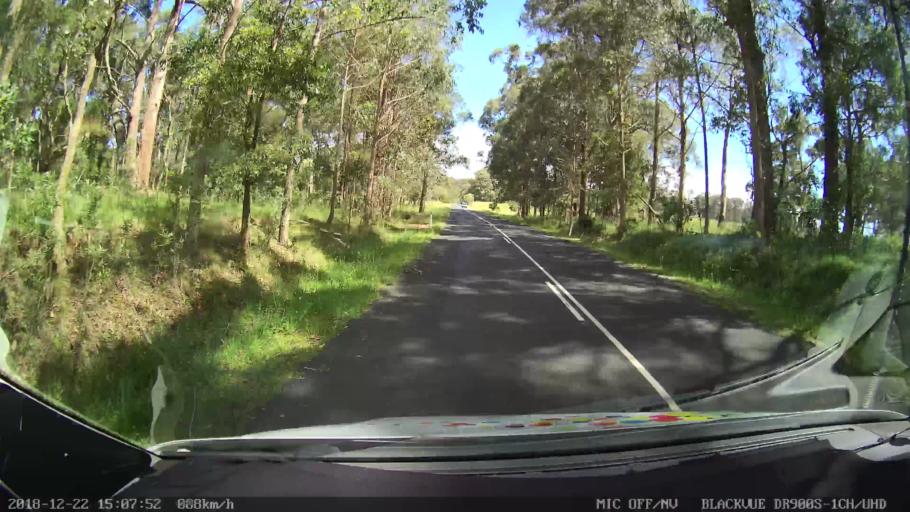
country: AU
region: New South Wales
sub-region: Bellingen
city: Dorrigo
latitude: -30.3048
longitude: 152.4126
